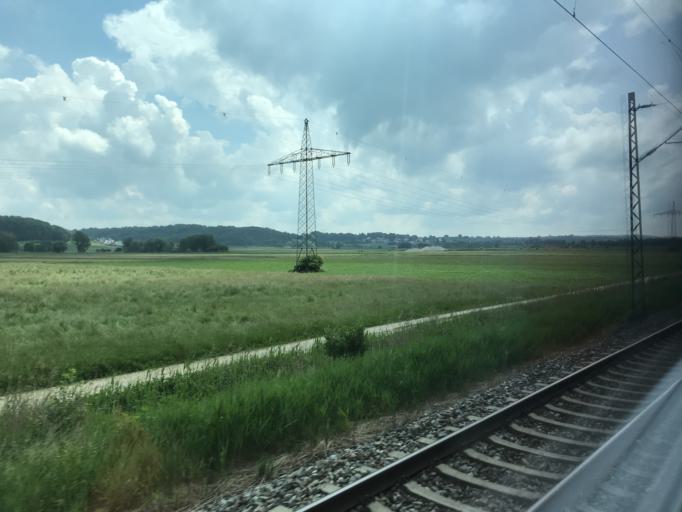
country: DE
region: Bavaria
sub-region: Swabia
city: Burgau
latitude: 48.4373
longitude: 10.4193
